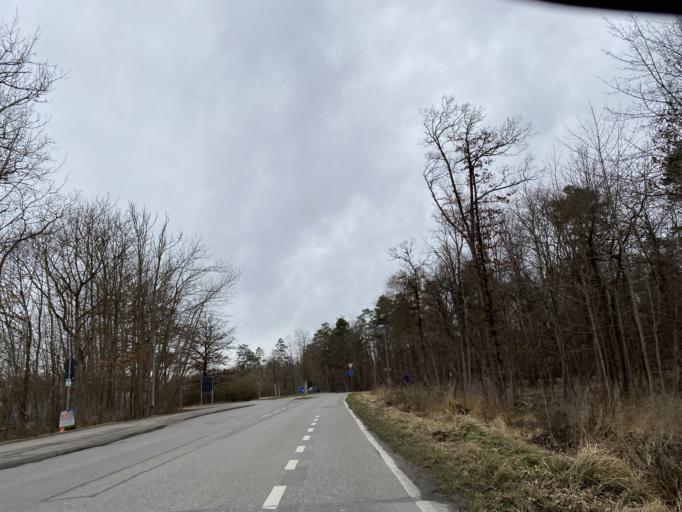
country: DE
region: Bavaria
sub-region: Upper Bavaria
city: Fuerstenfeldbruck
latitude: 48.1943
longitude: 11.2575
